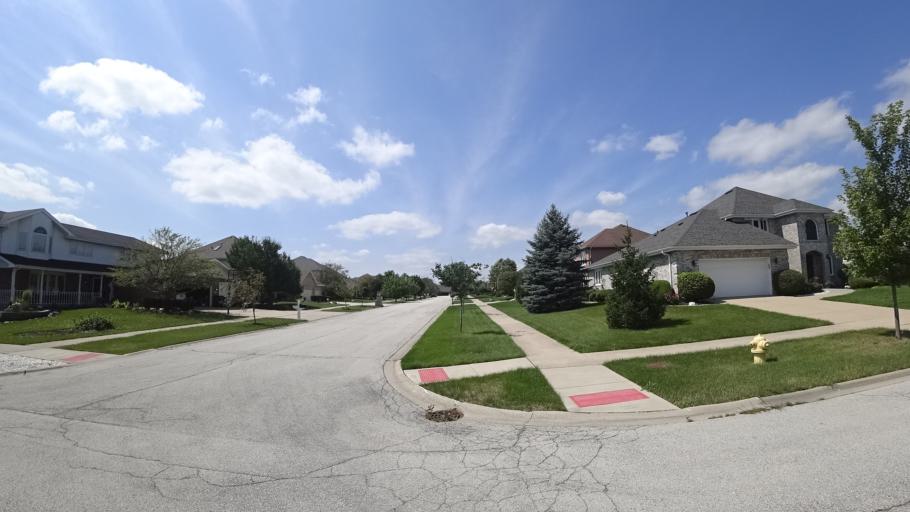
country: US
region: Illinois
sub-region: Cook County
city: Orland Hills
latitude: 41.5657
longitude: -87.8411
